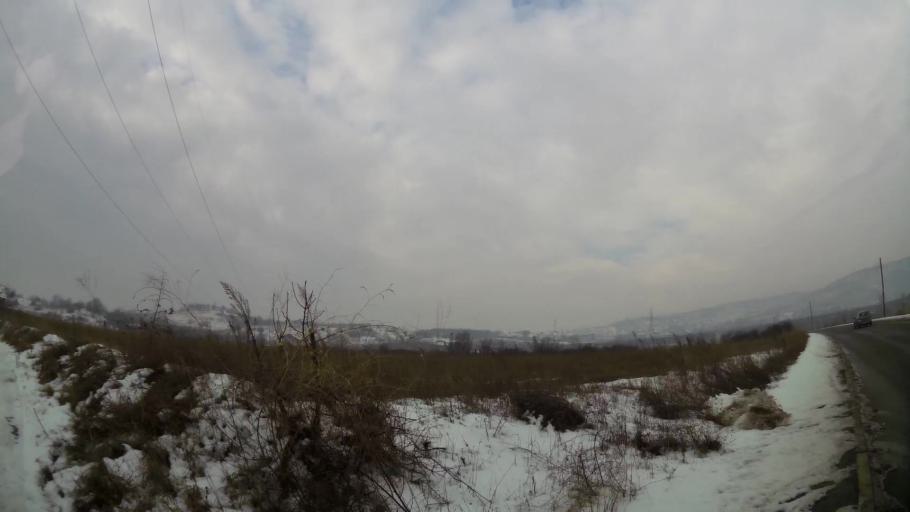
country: MK
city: Kondovo
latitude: 42.0368
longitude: 21.3389
